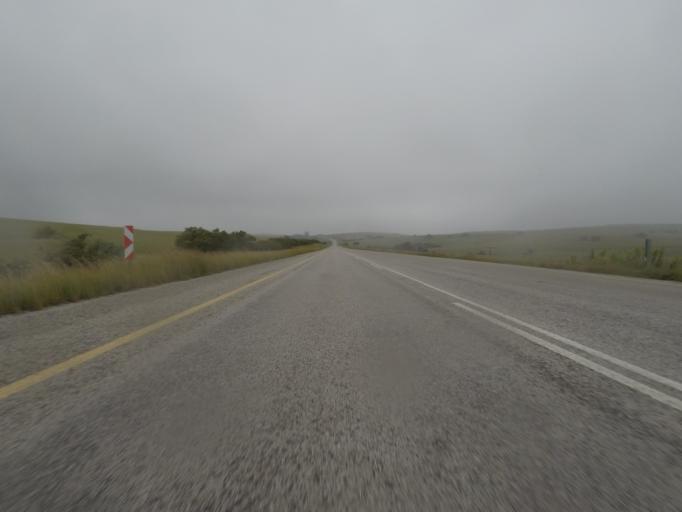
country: ZA
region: Eastern Cape
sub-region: Cacadu District Municipality
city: Grahamstown
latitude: -33.6292
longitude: 26.3116
